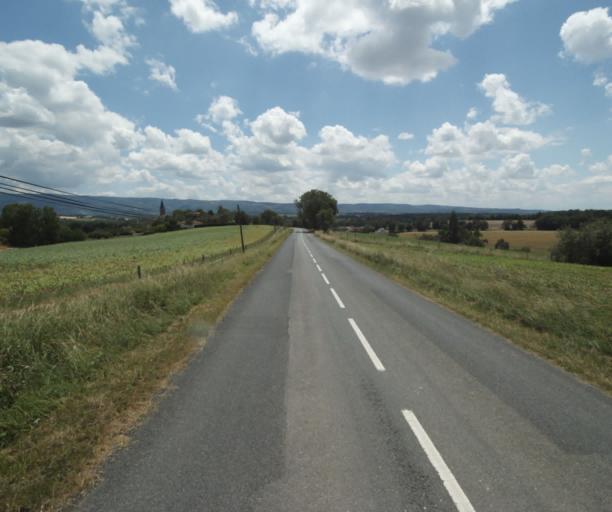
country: FR
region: Midi-Pyrenees
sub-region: Departement du Tarn
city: Soual
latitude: 43.5330
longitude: 2.0617
